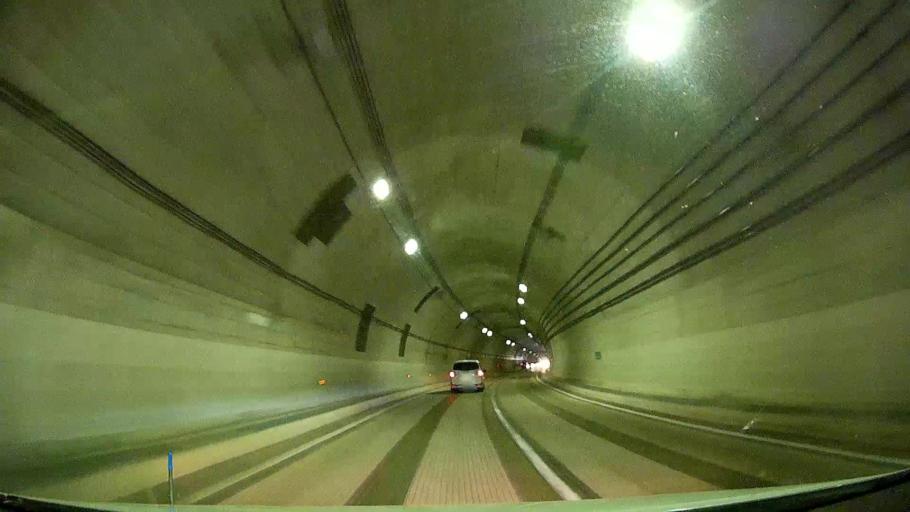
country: JP
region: Ishikawa
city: Nanao
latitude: 37.4751
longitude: 137.0939
